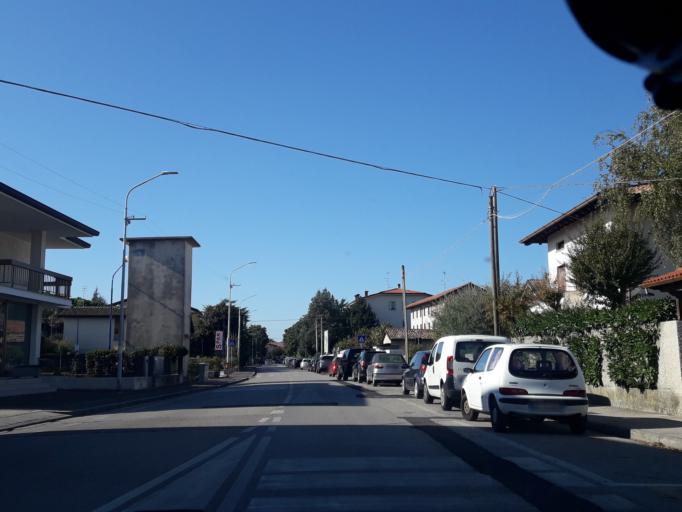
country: IT
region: Friuli Venezia Giulia
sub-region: Provincia di Udine
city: Udine
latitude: 46.0647
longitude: 13.2579
